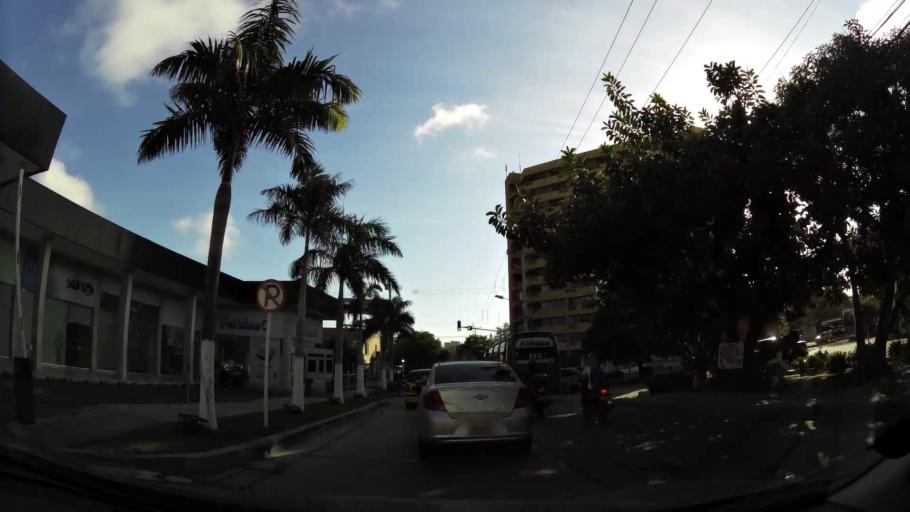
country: CO
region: Atlantico
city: Barranquilla
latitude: 11.0009
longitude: -74.8166
